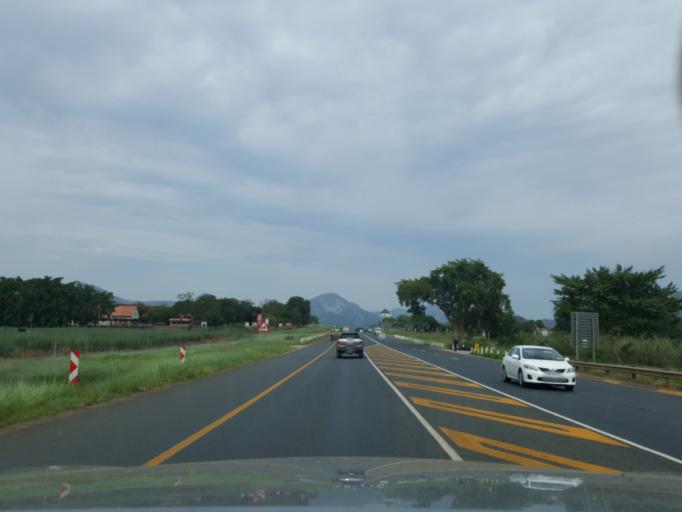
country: SZ
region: Hhohho
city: Ntfonjeni
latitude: -25.5366
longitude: 31.3361
